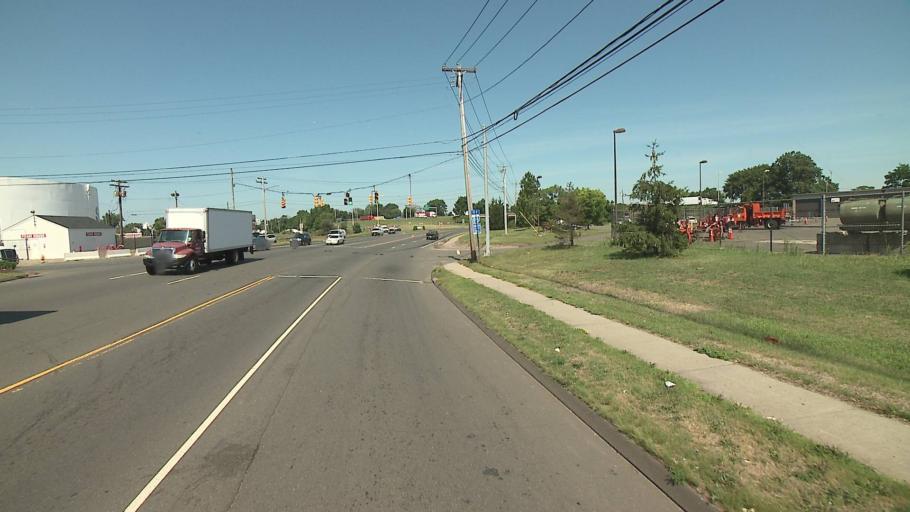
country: US
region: Connecticut
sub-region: Fairfield County
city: Stratford
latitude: 41.1731
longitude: -73.1574
